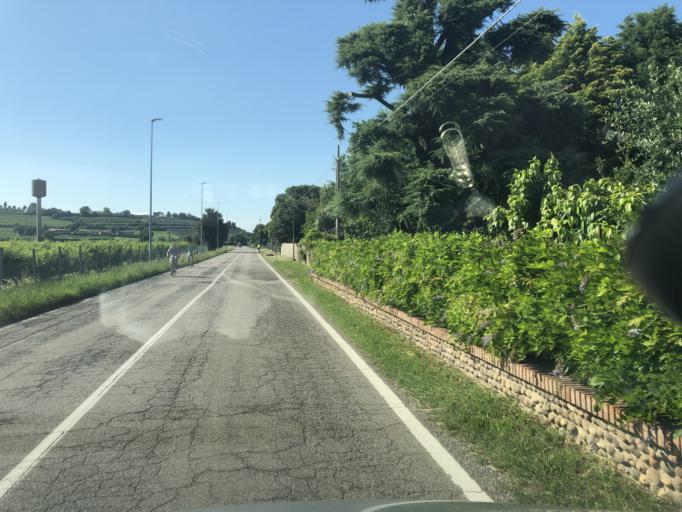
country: IT
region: Veneto
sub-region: Provincia di Verona
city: Villafranca di Verona
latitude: 45.3750
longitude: 10.8288
